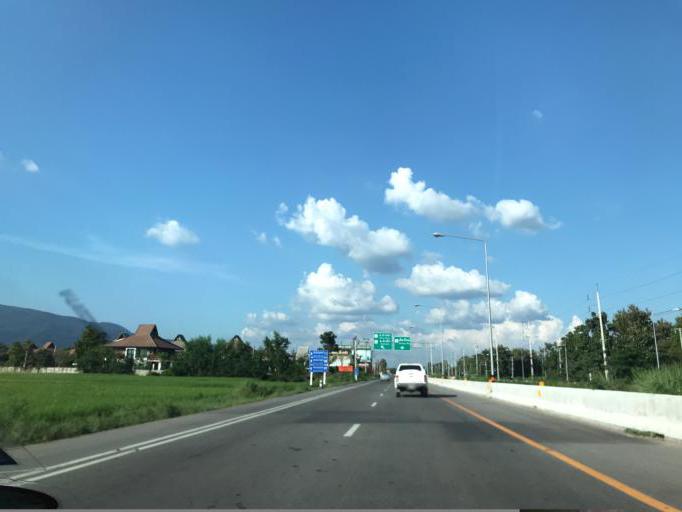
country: TH
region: Chiang Mai
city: Hang Dong
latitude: 18.7145
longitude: 98.9258
